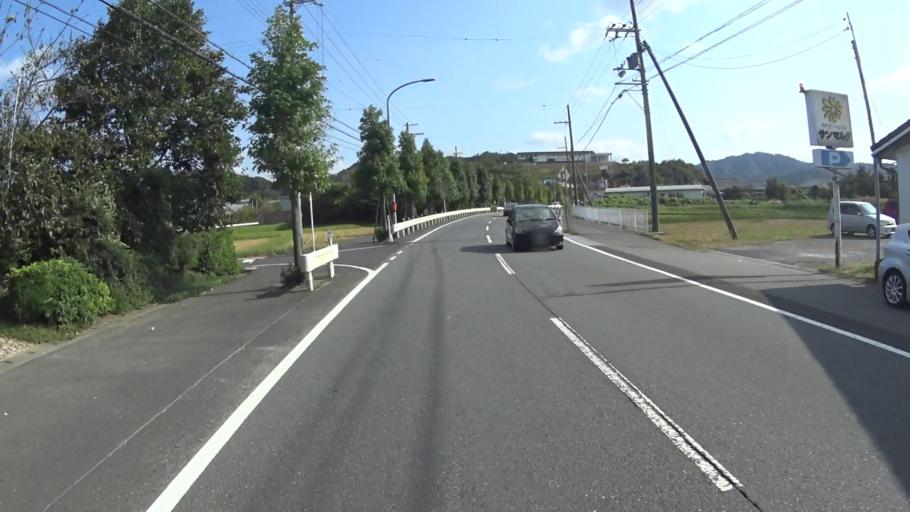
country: JP
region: Kyoto
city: Miyazu
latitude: 35.5835
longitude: 135.0997
